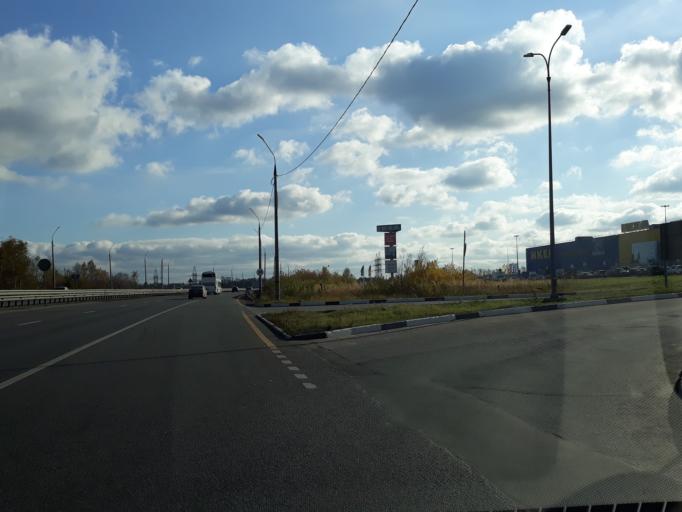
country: RU
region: Nizjnij Novgorod
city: Afonino
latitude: 56.2274
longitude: 44.0746
